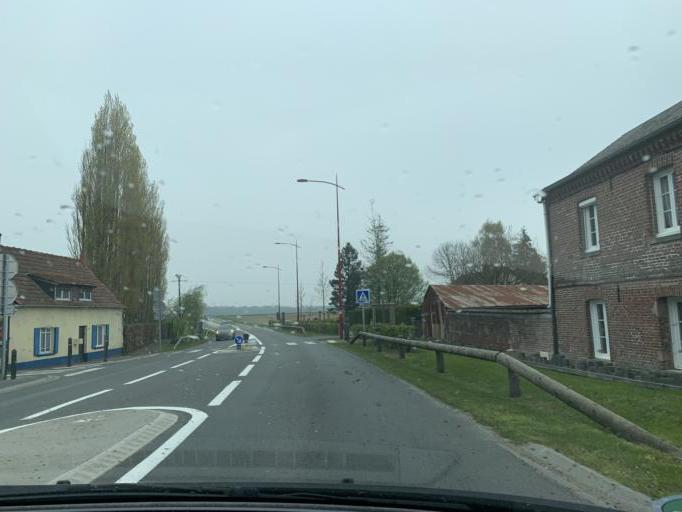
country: FR
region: Picardie
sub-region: Departement de la Somme
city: Nouvion
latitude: 50.1741
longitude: 1.8094
